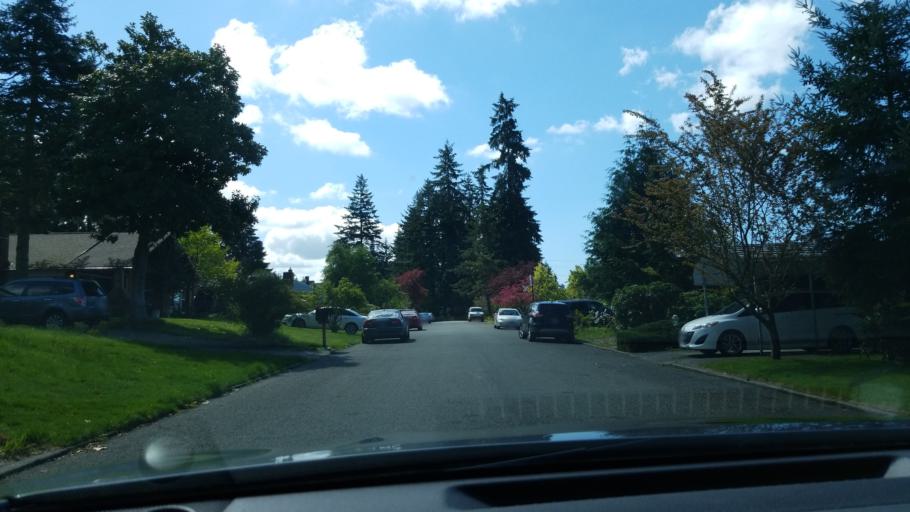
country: US
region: Washington
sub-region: King County
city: Shoreline
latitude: 47.7469
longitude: -122.3436
